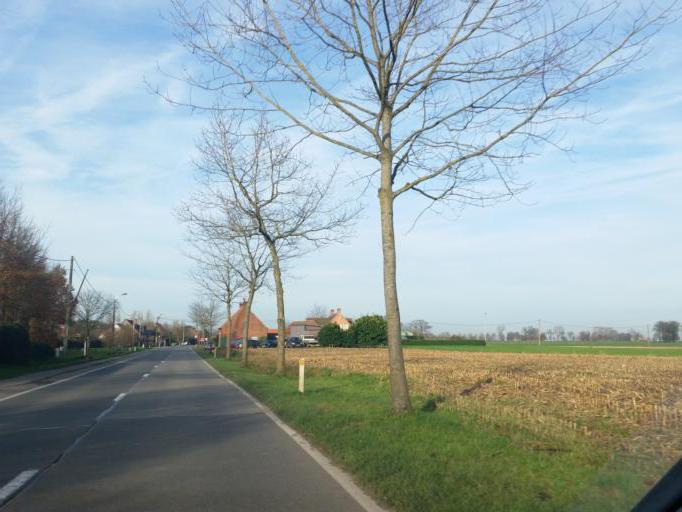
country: BE
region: Flanders
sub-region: Provincie West-Vlaanderen
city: Beernem
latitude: 51.1602
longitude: 3.3676
